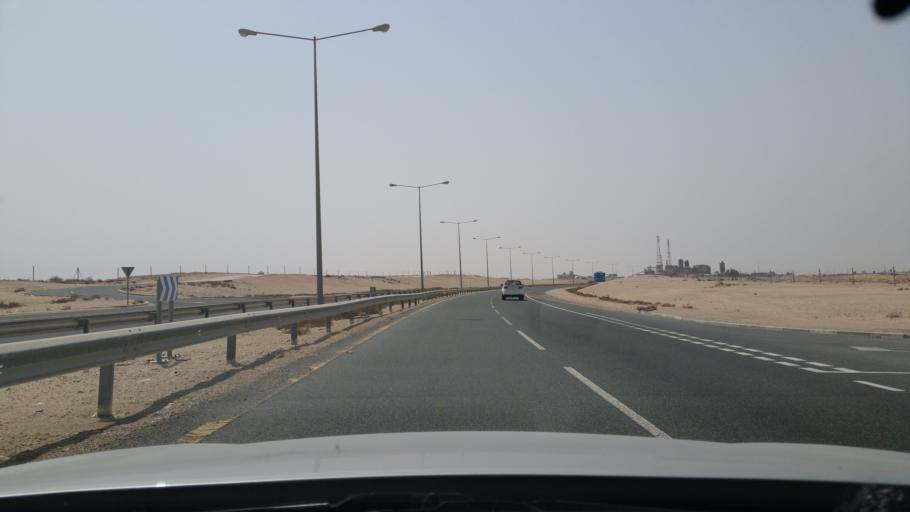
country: QA
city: Umm Bab
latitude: 25.2220
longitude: 50.8071
